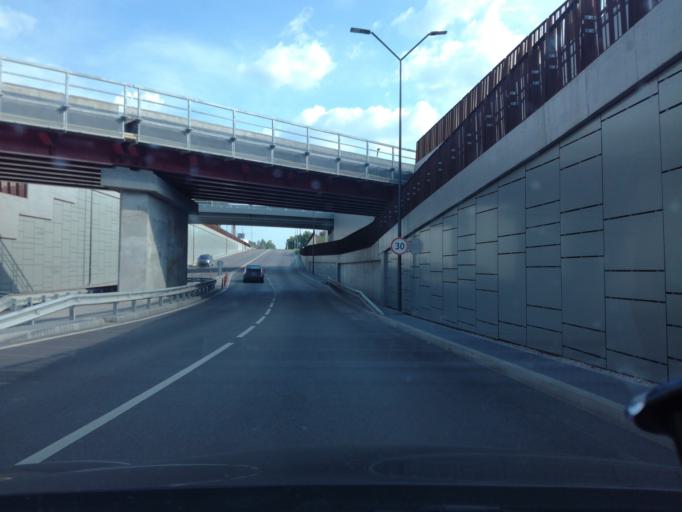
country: LT
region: Marijampoles apskritis
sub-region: Marijampole Municipality
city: Marijampole
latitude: 54.5384
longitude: 23.3507
